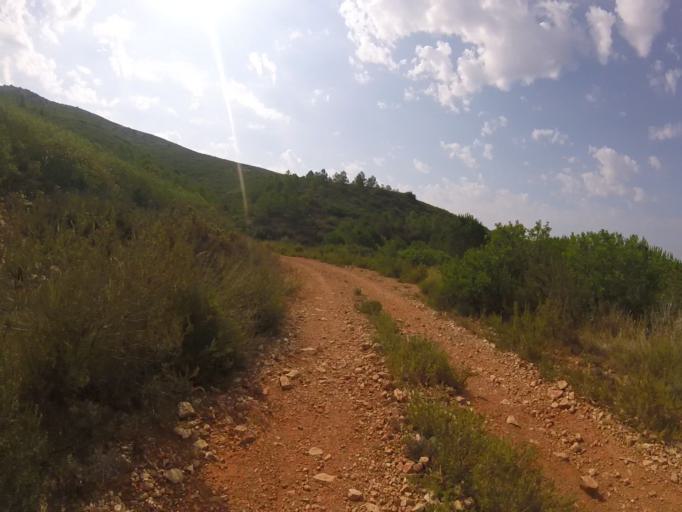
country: ES
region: Valencia
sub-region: Provincia de Castello
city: Alcala de Xivert
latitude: 40.3500
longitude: 0.1986
